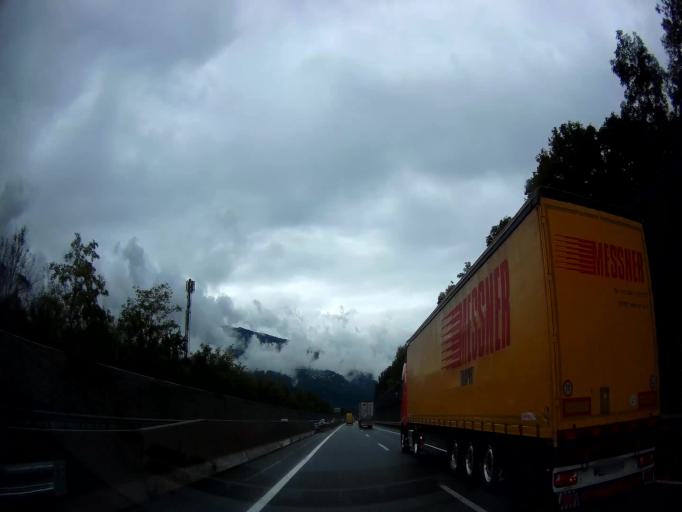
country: AT
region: Tyrol
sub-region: Politischer Bezirk Schwaz
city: Vomp
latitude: 47.3403
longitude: 11.6875
